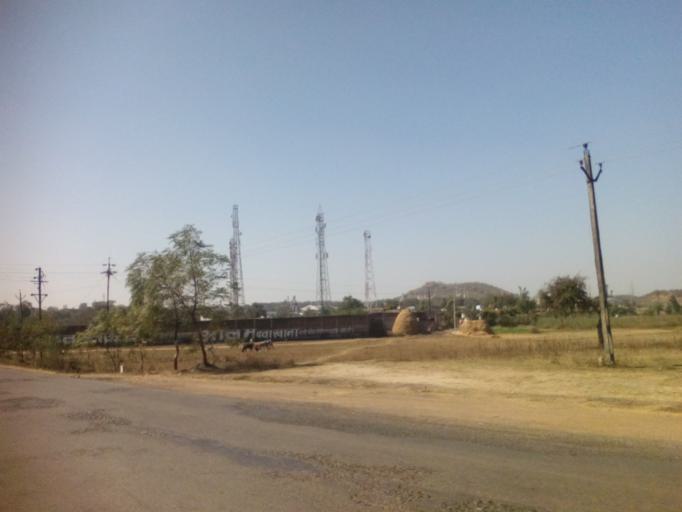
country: IN
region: Maharashtra
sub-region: Gondiya
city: Gondia
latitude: 21.4710
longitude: 80.1406
